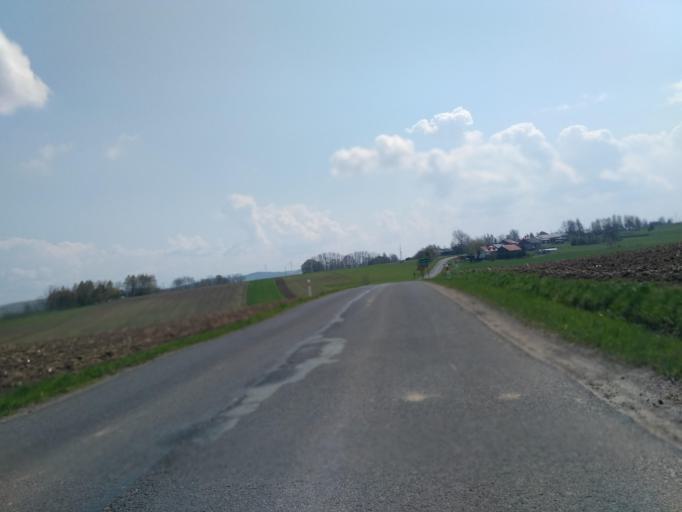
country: PL
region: Subcarpathian Voivodeship
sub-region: Powiat sanocki
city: Zarszyn
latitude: 49.5257
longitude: 21.9912
